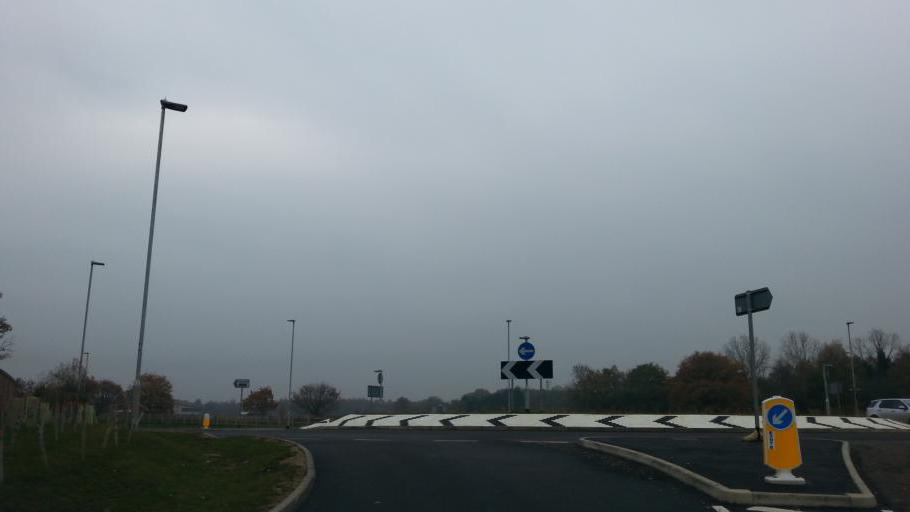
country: GB
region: England
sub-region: Suffolk
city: Thurston
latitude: 52.2457
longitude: 0.7801
